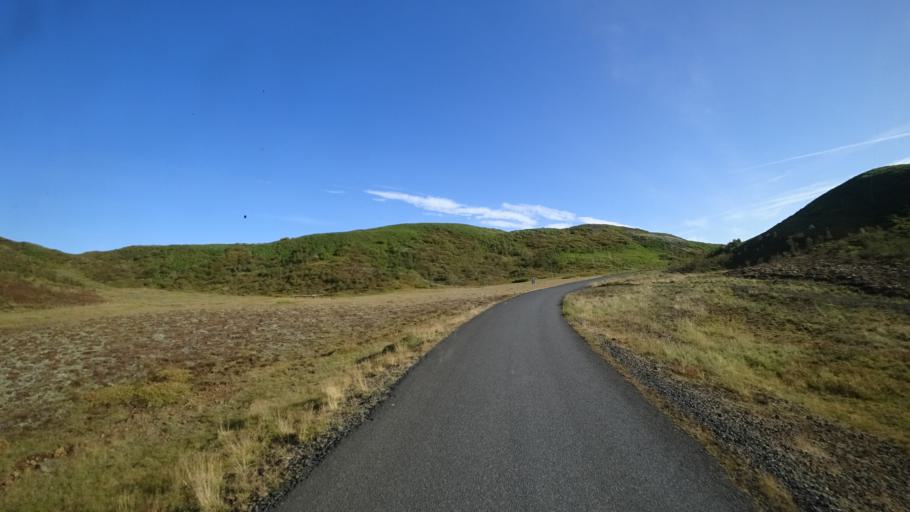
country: IS
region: South
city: Hveragerdi
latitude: 64.1378
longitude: -21.2523
